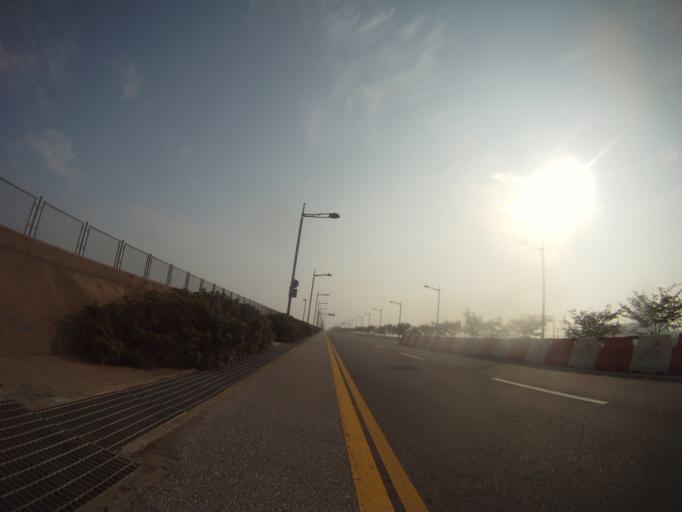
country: KR
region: Incheon
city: Incheon
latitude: 37.4326
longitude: 126.4624
